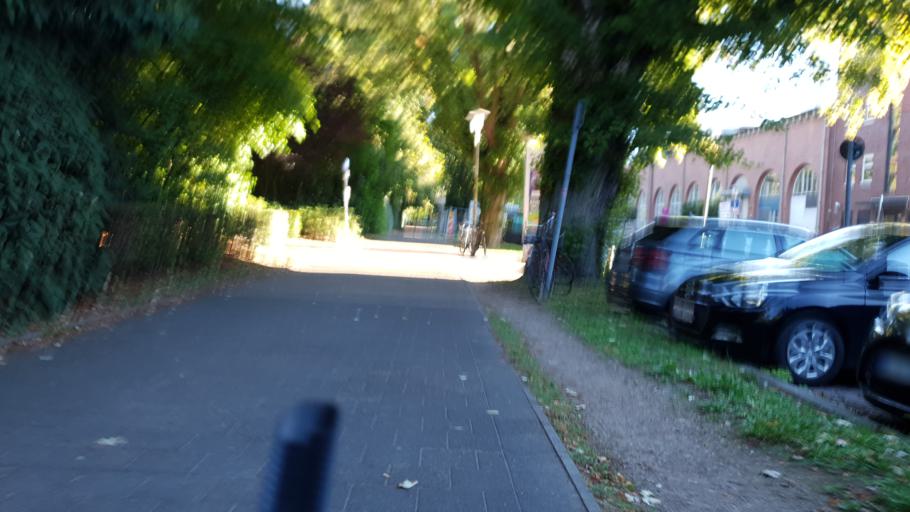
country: DE
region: Schleswig-Holstein
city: Kiel
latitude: 54.3269
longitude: 10.1254
